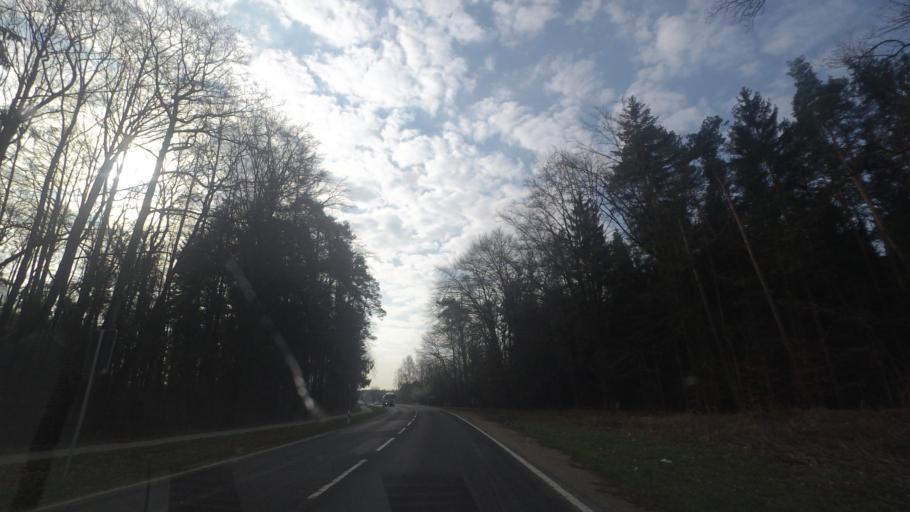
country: DE
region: Bavaria
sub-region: Regierungsbezirk Mittelfranken
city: Altdorf
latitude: 49.4066
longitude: 11.3439
